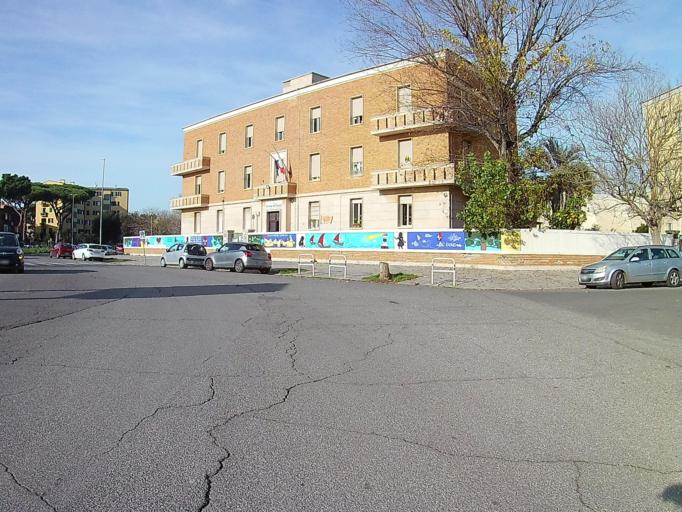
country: IT
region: Latium
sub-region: Citta metropolitana di Roma Capitale
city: Lido di Ostia
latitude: 41.7279
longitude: 12.2968
